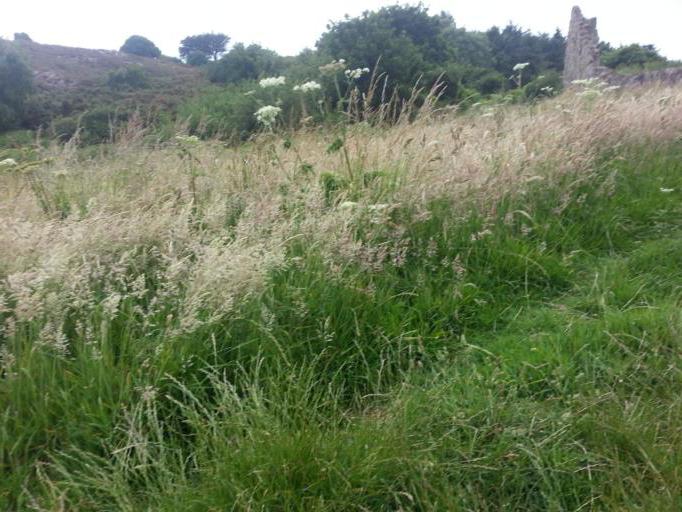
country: IE
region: Leinster
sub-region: Wicklow
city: Bray
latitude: 53.1940
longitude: -6.0902
